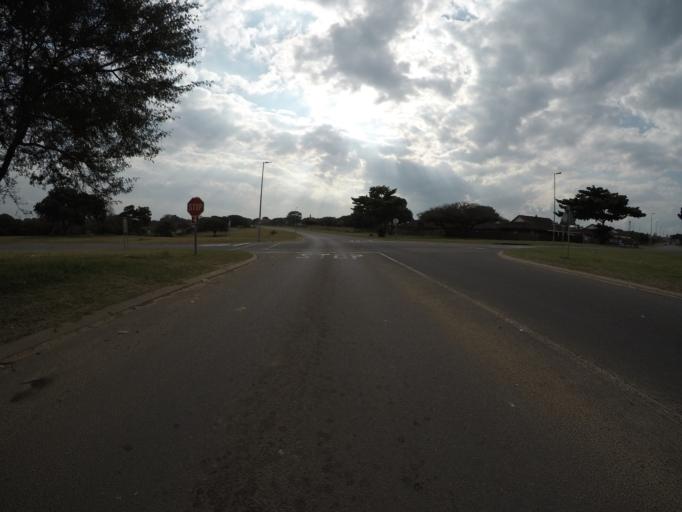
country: ZA
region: KwaZulu-Natal
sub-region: uThungulu District Municipality
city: Richards Bay
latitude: -28.7426
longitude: 32.0822
